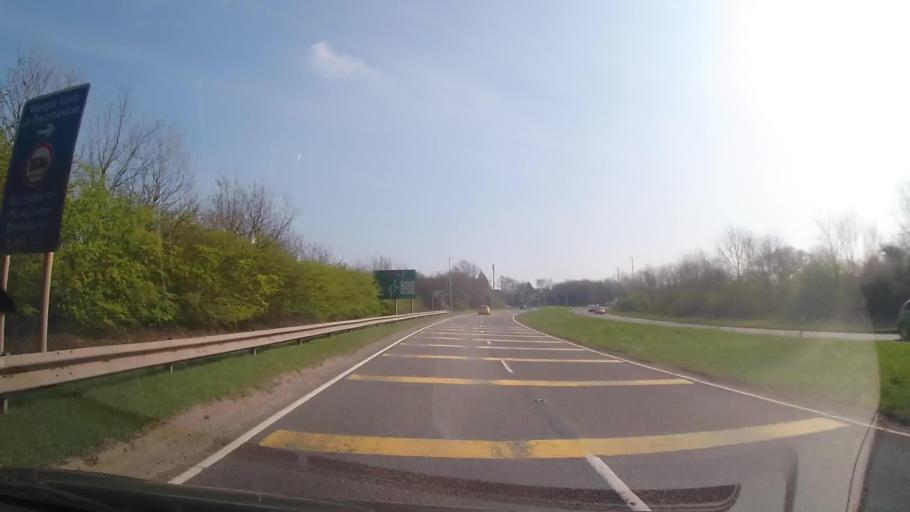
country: GB
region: England
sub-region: Leicestershire
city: Markfield
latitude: 52.6885
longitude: -1.2692
